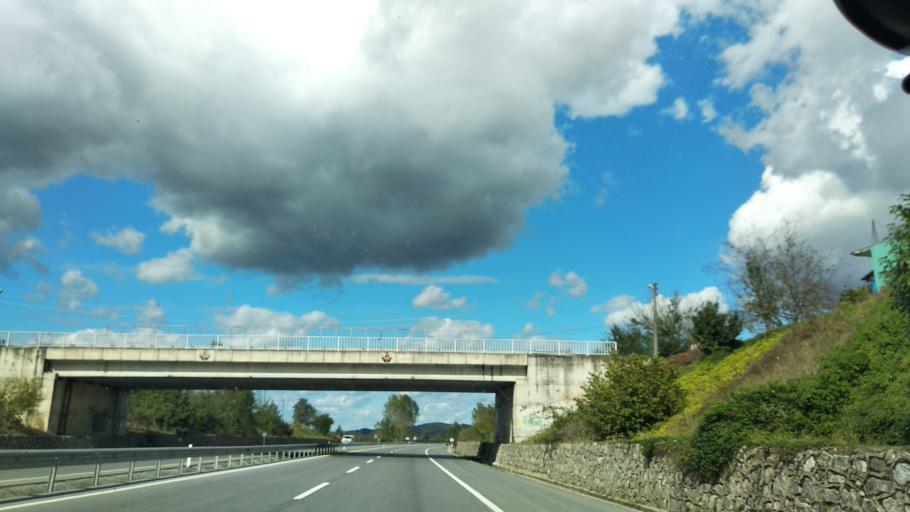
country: TR
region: Sakarya
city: Ortakoy
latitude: 41.0230
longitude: 30.6140
